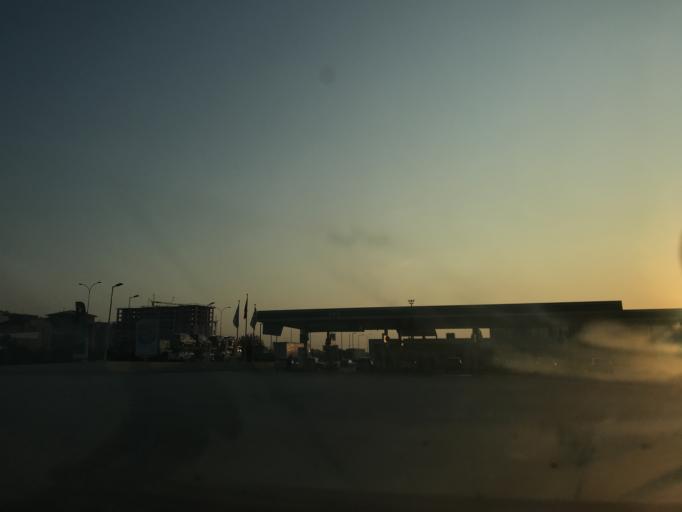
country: TR
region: Kocaeli
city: Korfez
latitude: 40.7691
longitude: 29.7983
